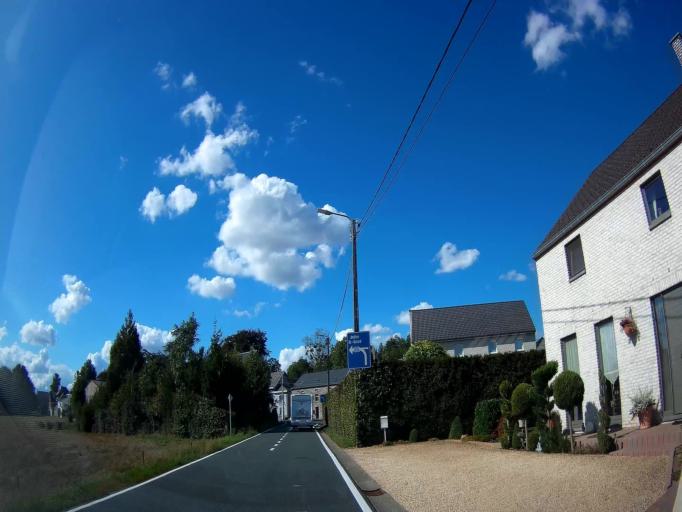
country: BE
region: Wallonia
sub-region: Province de Namur
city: Mettet
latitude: 50.3171
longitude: 4.7558
